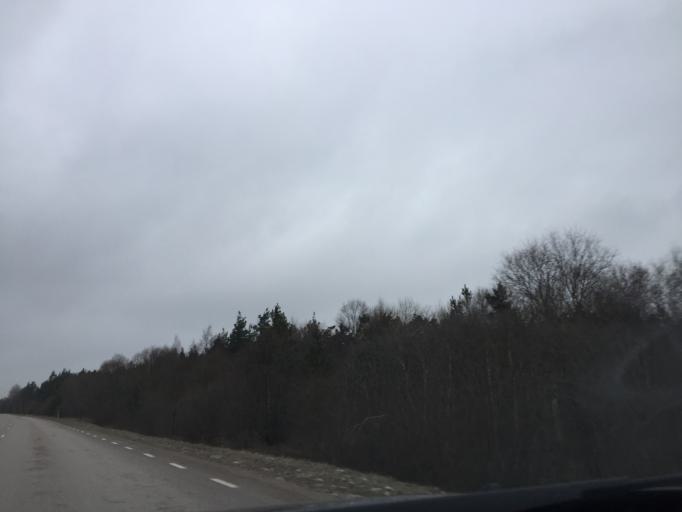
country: EE
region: Saare
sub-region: Kuressaare linn
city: Kuressaare
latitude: 58.2845
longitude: 22.4204
